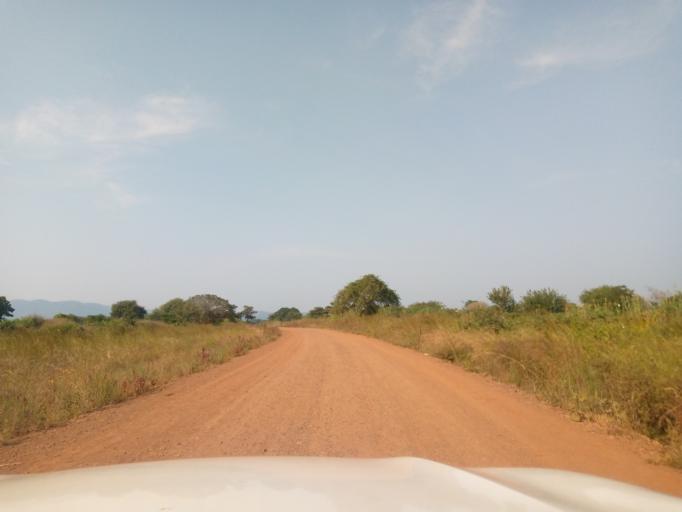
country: ET
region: Oromiya
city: Mendi
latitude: 10.1436
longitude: 34.9508
